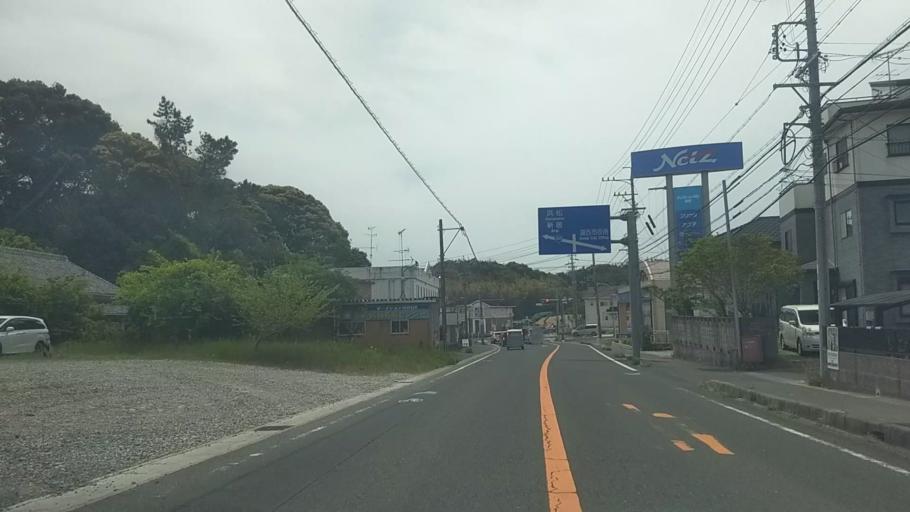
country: JP
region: Shizuoka
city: Kosai-shi
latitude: 34.7058
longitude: 137.5501
